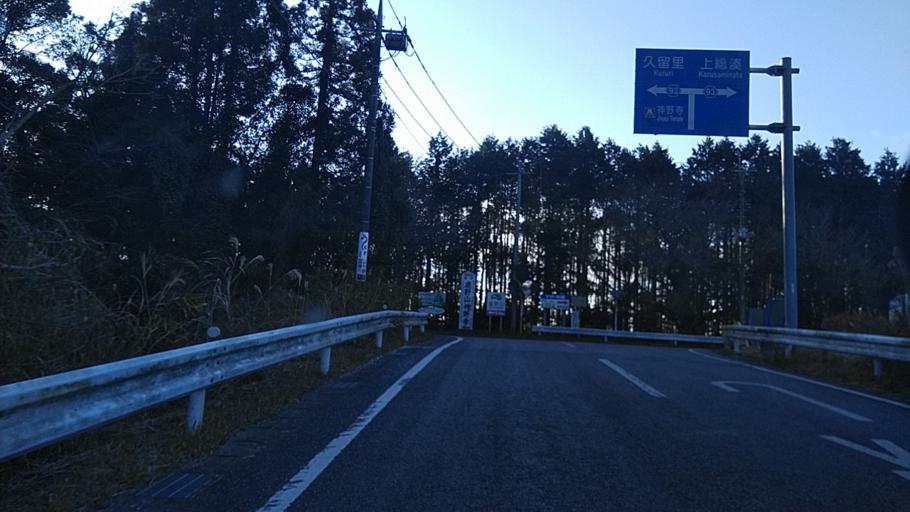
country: JP
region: Chiba
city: Kimitsu
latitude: 35.2534
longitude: 139.9545
